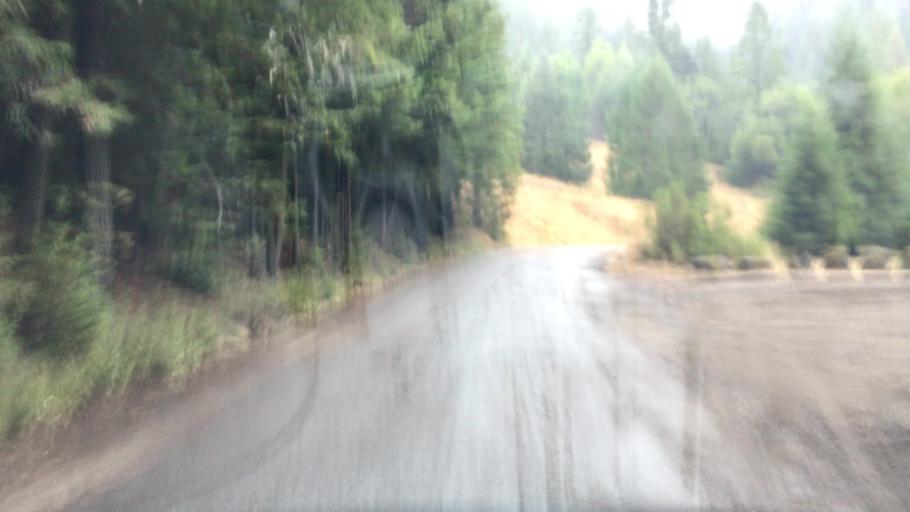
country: US
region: California
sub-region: Humboldt County
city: Rio Dell
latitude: 40.3524
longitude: -123.9863
